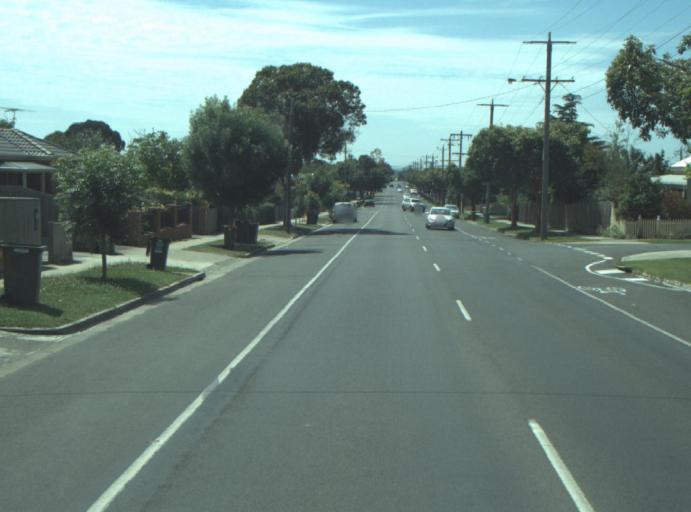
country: AU
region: Victoria
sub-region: Greater Geelong
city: Hamlyn Heights
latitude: -38.1395
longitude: 144.3195
